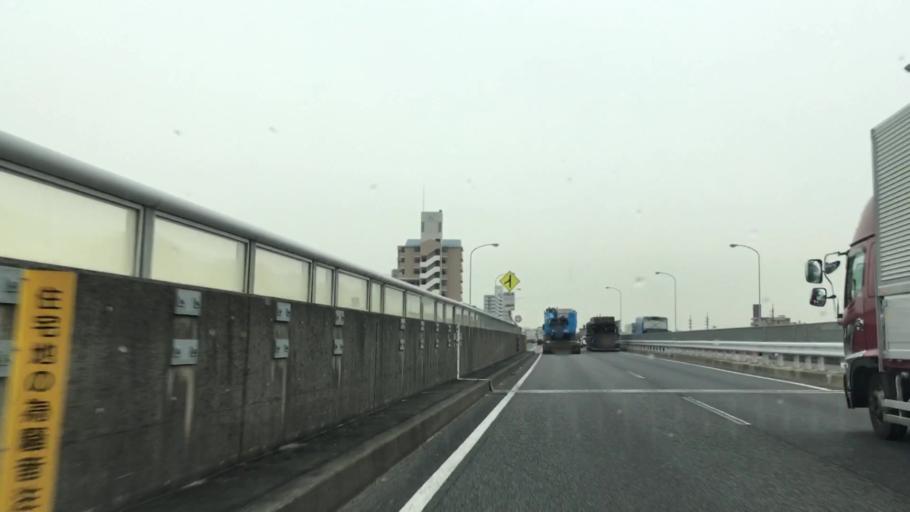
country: JP
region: Aichi
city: Chiryu
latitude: 34.9763
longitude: 137.0359
